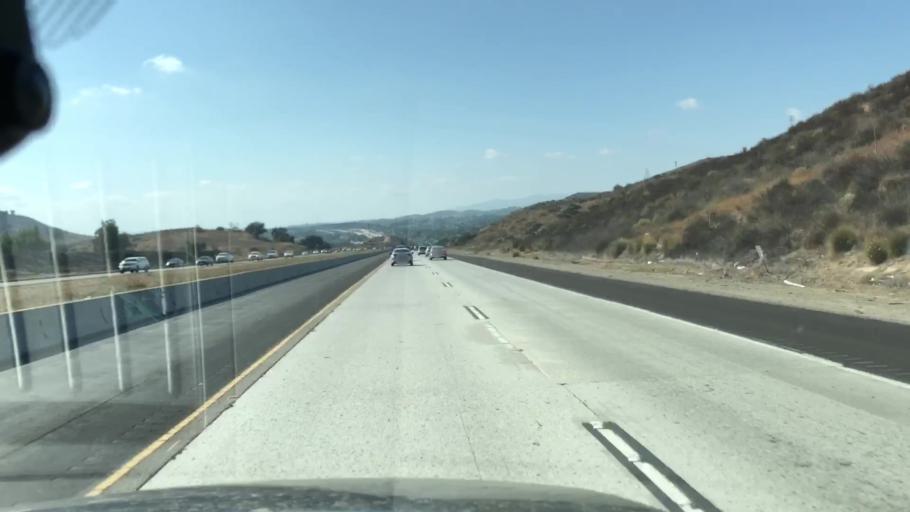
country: US
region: California
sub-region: Ventura County
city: Simi Valley
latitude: 34.2921
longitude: -118.8258
